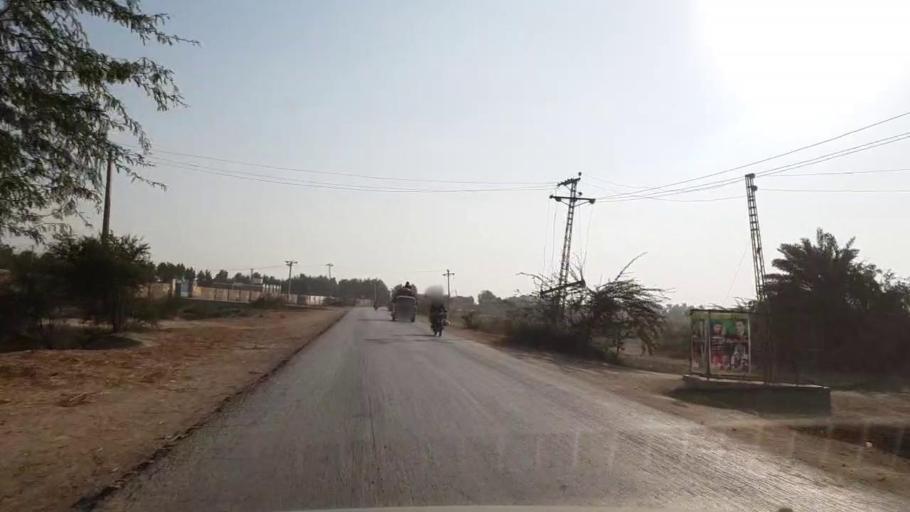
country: PK
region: Sindh
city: Bulri
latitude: 24.8664
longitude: 68.3378
